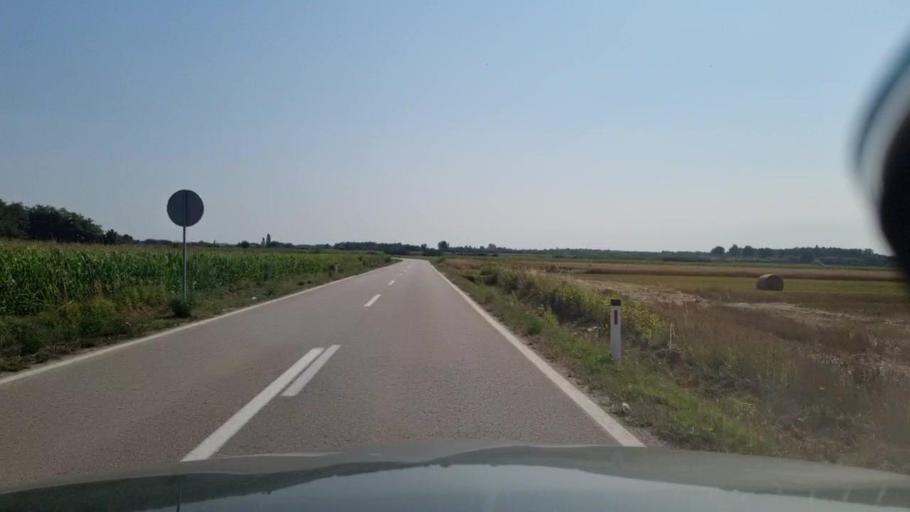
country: BA
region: Federation of Bosnia and Herzegovina
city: Mionica
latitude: 44.8726
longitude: 18.5115
